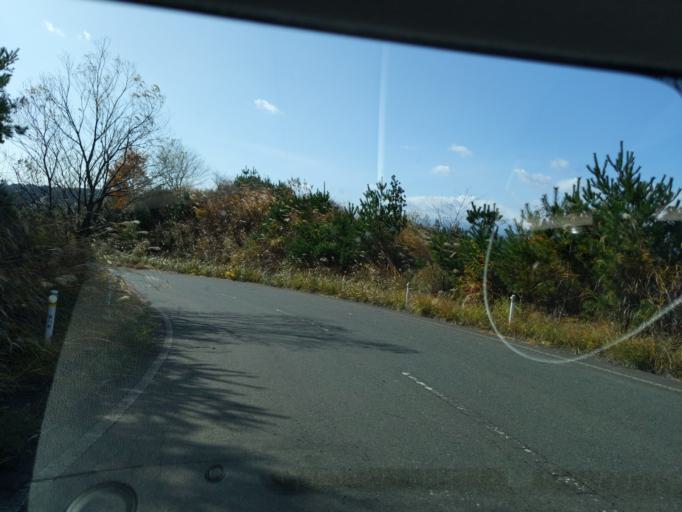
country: JP
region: Iwate
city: Mizusawa
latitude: 39.0366
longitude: 141.0821
